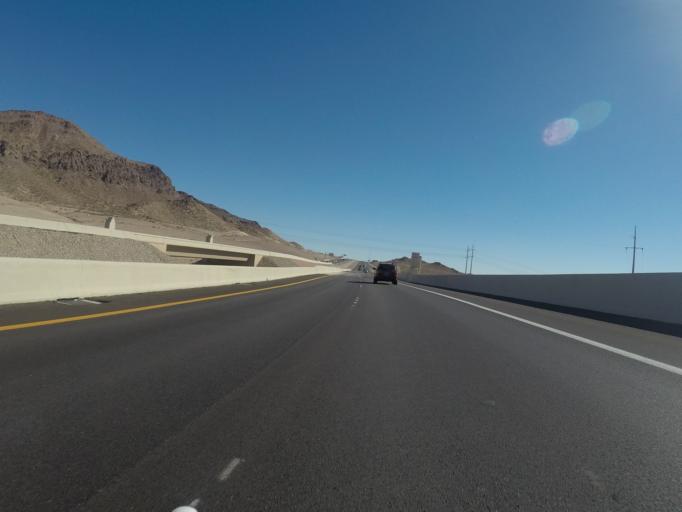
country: US
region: Nevada
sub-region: Clark County
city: Boulder City
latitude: 35.9682
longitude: -114.9110
